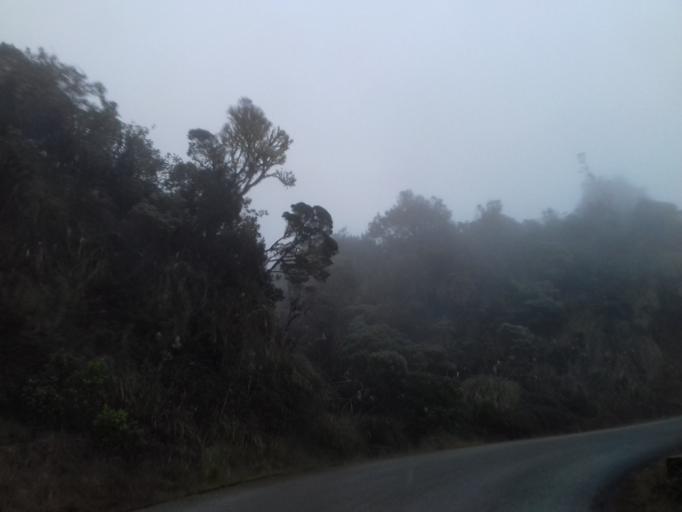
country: CO
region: Tolima
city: Herveo
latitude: 4.9992
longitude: -75.3276
